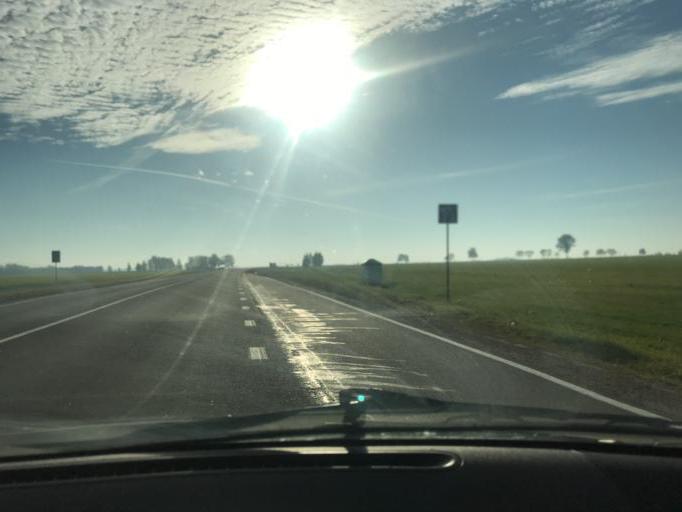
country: BY
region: Brest
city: Drahichyn
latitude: 52.2070
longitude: 25.2214
